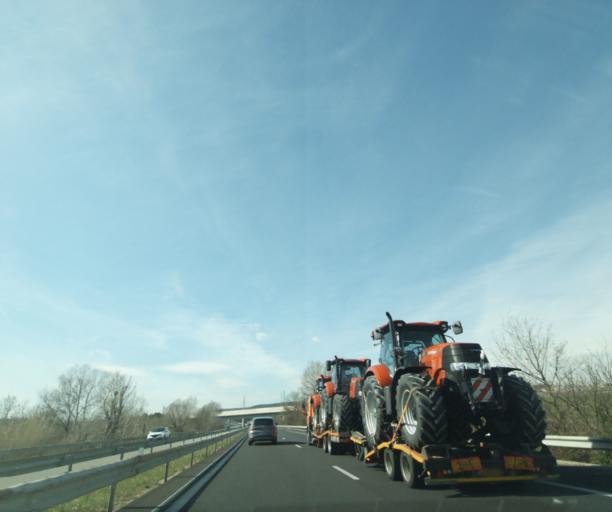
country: FR
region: Languedoc-Roussillon
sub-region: Departement du Gard
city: Roquemaure
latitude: 44.0289
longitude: 4.7482
